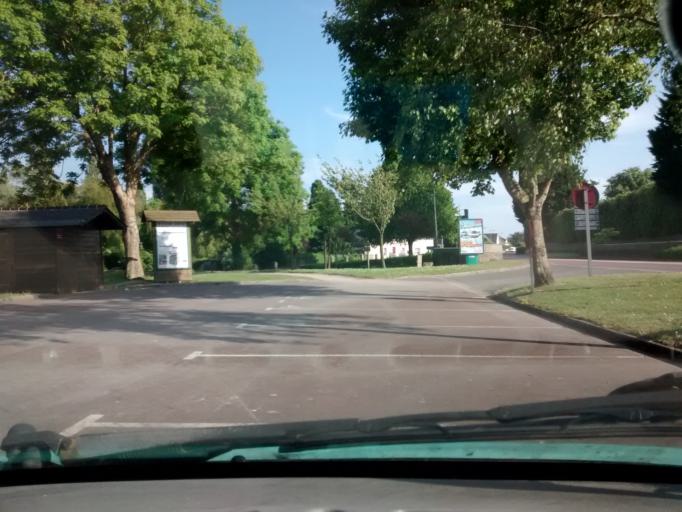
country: FR
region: Lower Normandy
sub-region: Departement de la Manche
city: Lessay
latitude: 49.2217
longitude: -1.5319
